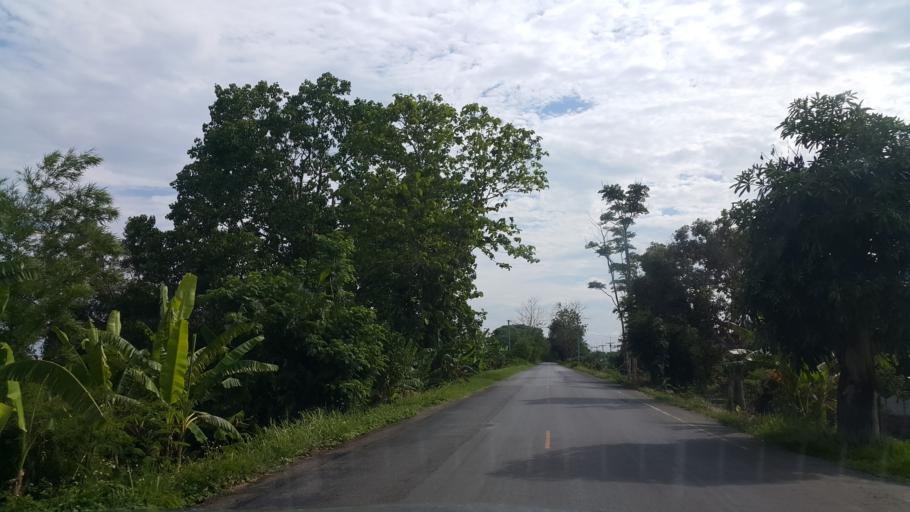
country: TH
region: Chiang Rai
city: Wiang Chai
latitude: 19.9527
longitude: 99.9318
